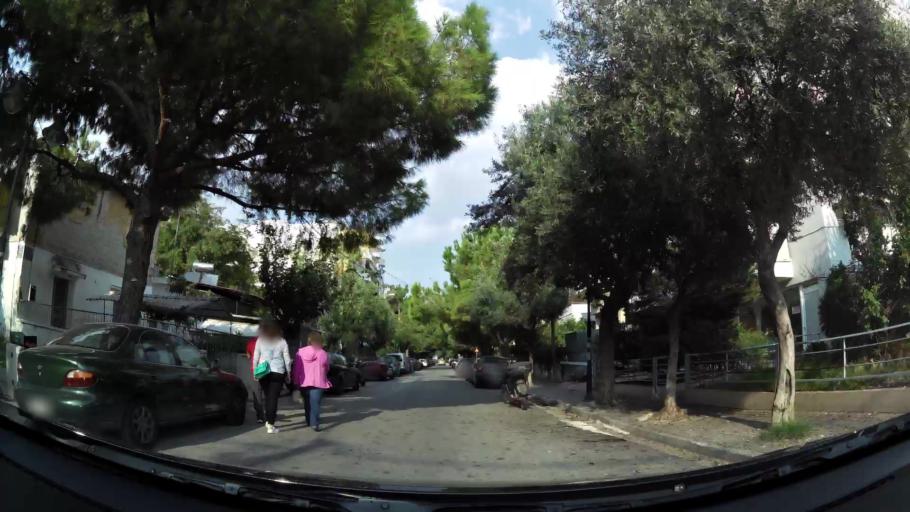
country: GR
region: Attica
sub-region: Nomarchia Athinas
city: Moskhaton
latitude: 37.9444
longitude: 23.6890
